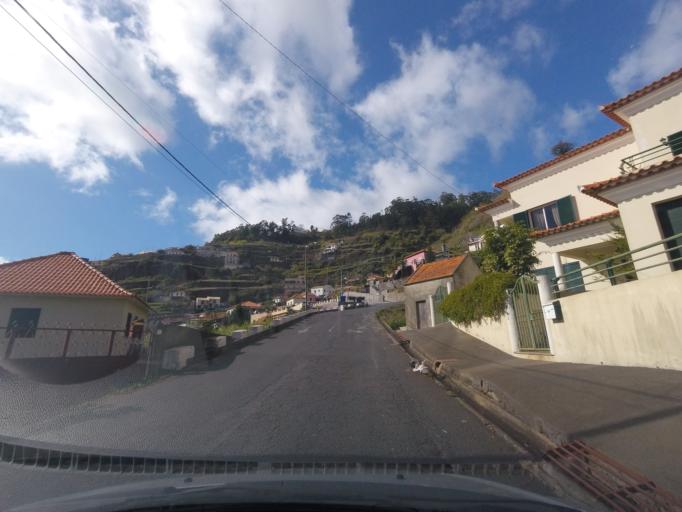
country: PT
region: Madeira
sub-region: Ribeira Brava
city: Campanario
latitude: 32.6611
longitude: -17.0107
